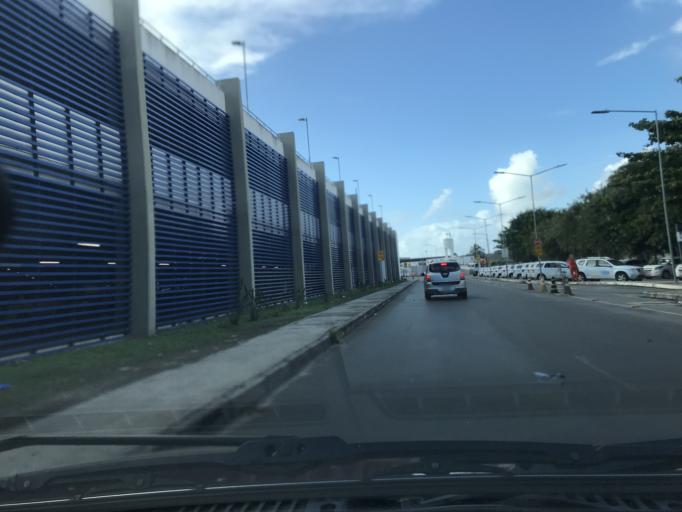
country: BR
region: Bahia
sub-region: Lauro De Freitas
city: Lauro de Freitas
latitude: -12.9142
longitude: -38.3363
